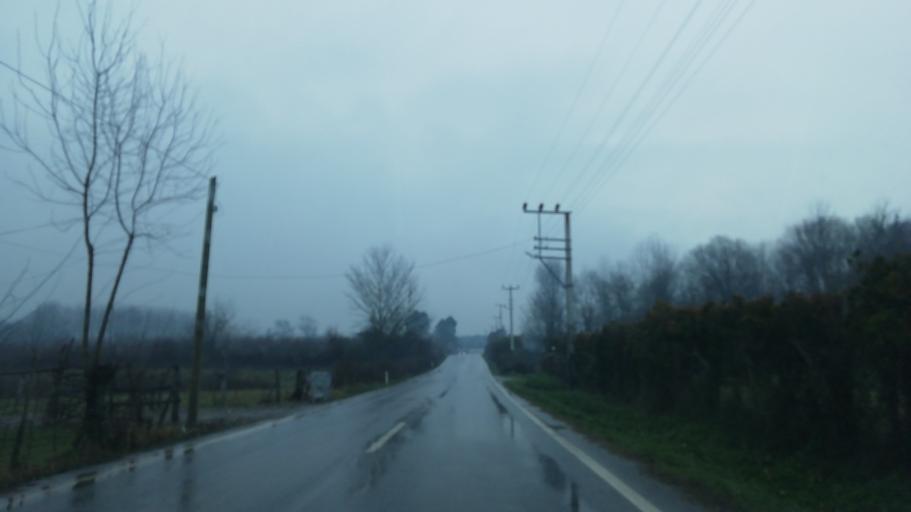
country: TR
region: Sakarya
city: Karapurcek
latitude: 40.6797
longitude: 30.5466
